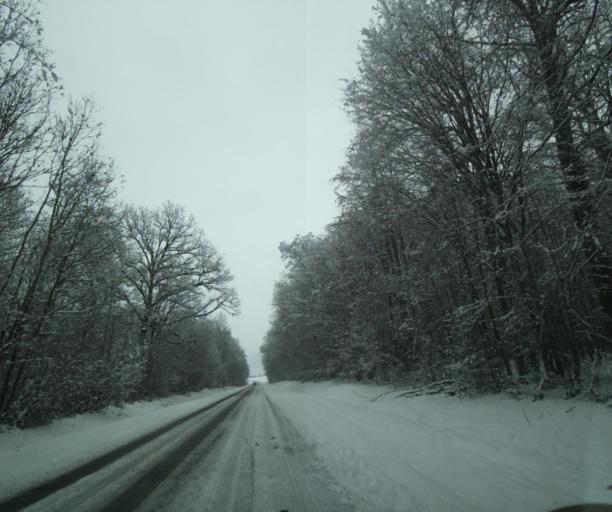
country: FR
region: Champagne-Ardenne
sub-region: Departement de la Haute-Marne
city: Montier-en-Der
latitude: 48.5263
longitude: 4.7972
